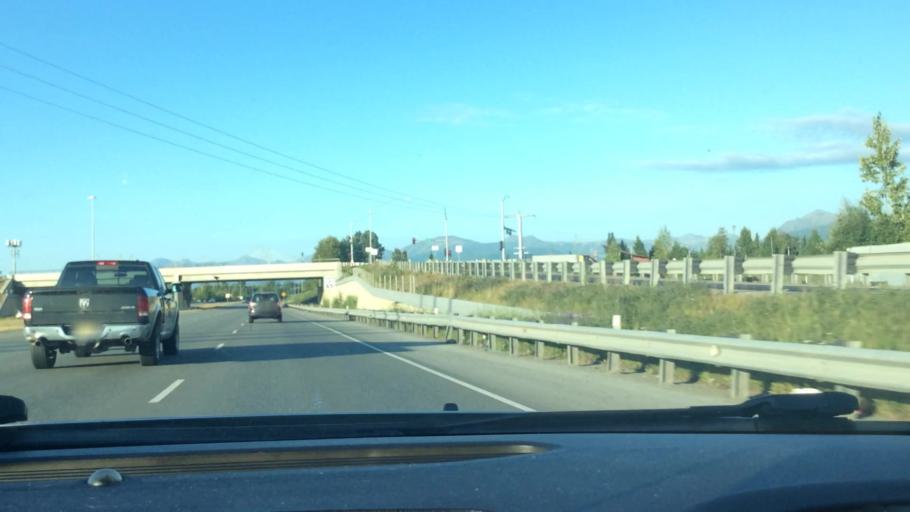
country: US
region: Alaska
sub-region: Anchorage Municipality
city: Anchorage
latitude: 61.2202
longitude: -149.8114
